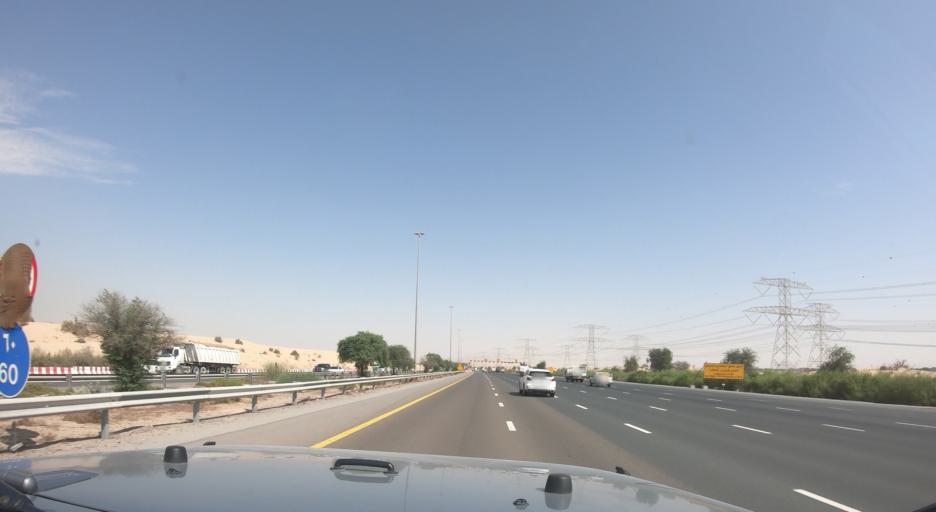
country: AE
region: Ash Shariqah
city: Sharjah
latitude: 25.1710
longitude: 55.5056
